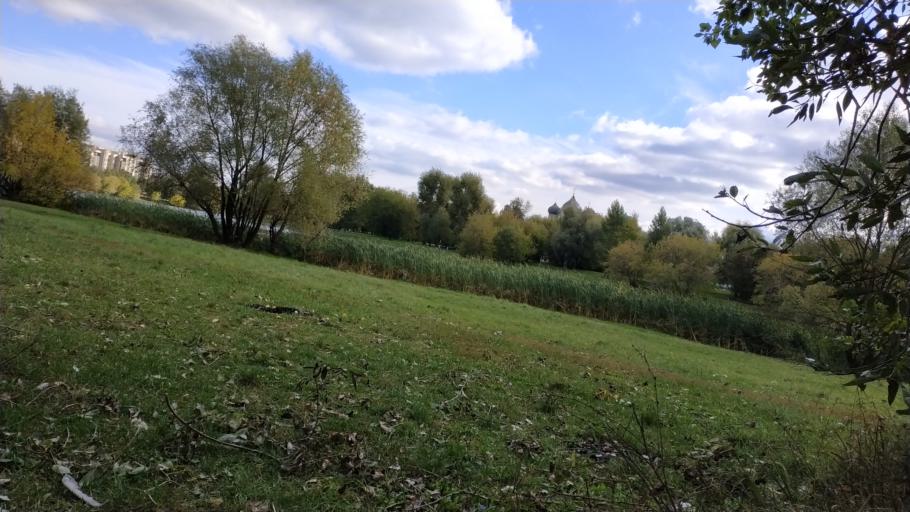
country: RU
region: Moscow
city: Metrogorodok
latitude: 55.7949
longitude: 37.7614
